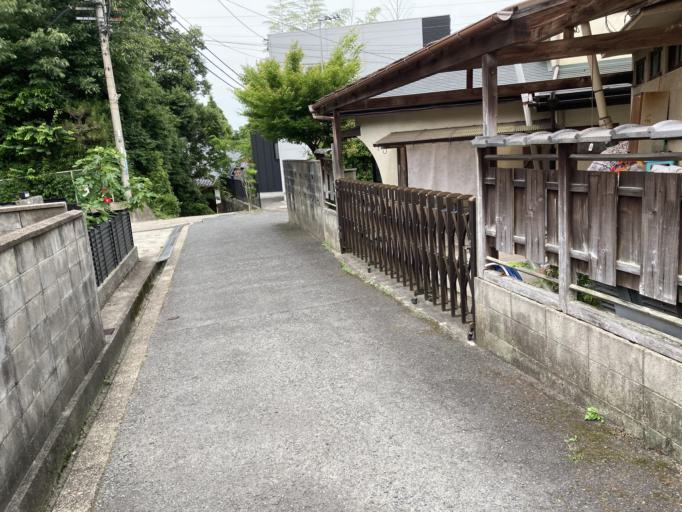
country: JP
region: Nara
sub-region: Ikoma-shi
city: Ikoma
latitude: 34.6993
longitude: 135.6927
